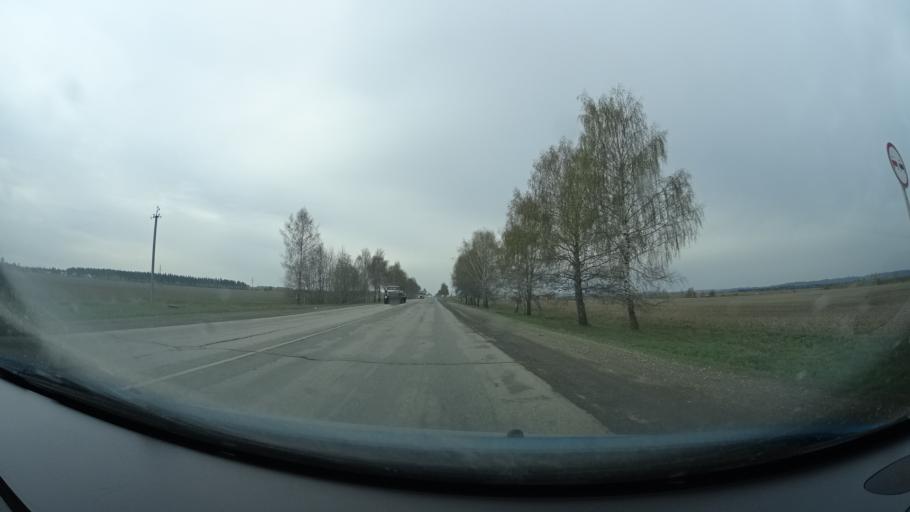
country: RU
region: Perm
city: Ust'-Kachka
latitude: 58.0724
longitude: 55.6357
